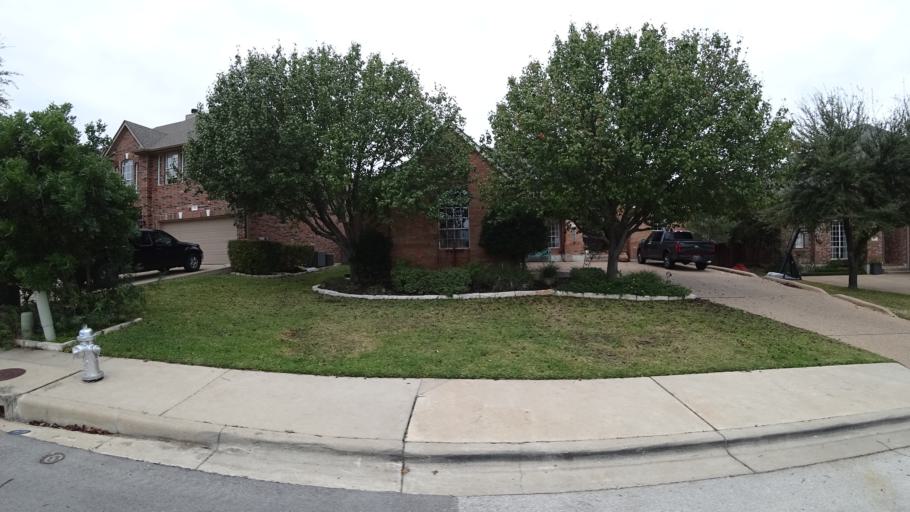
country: US
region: Texas
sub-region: Travis County
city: Bee Cave
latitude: 30.3152
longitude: -97.9291
